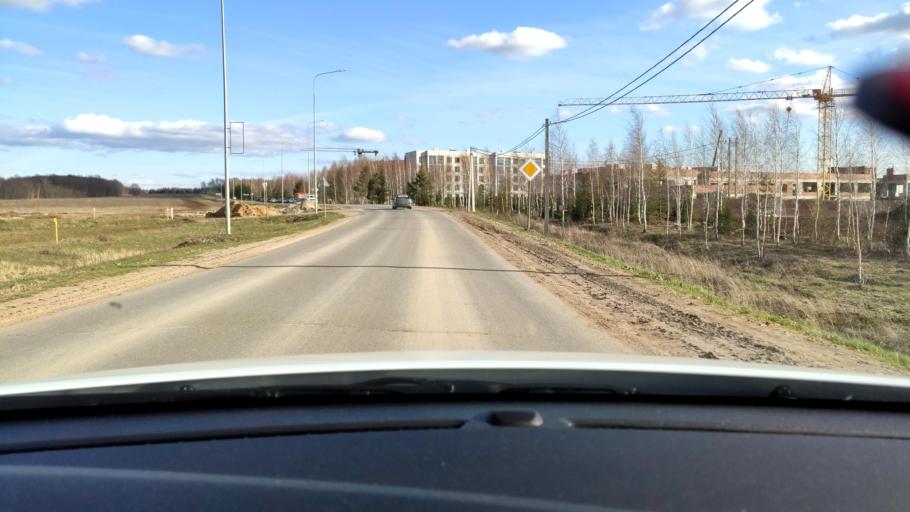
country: RU
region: Tatarstan
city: Vysokaya Gora
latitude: 55.9019
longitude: 49.3246
